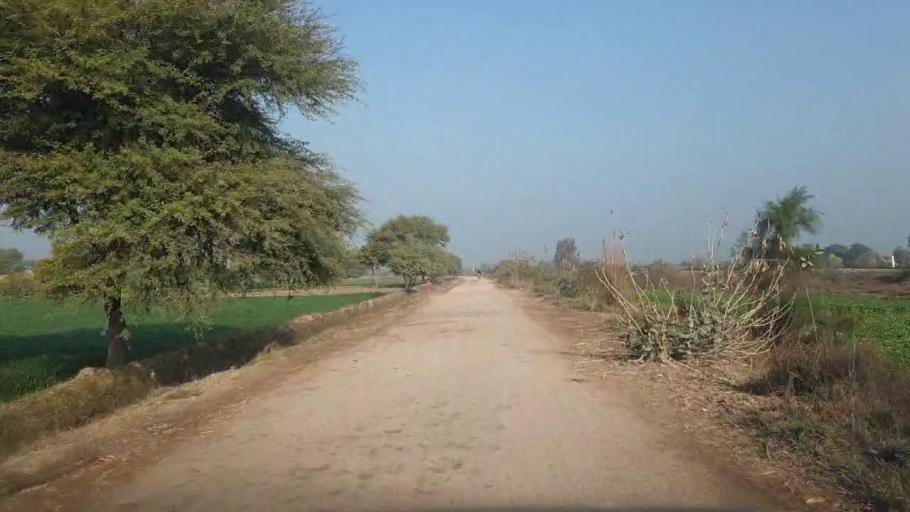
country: PK
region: Sindh
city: Shahdadpur
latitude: 25.9620
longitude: 68.6138
